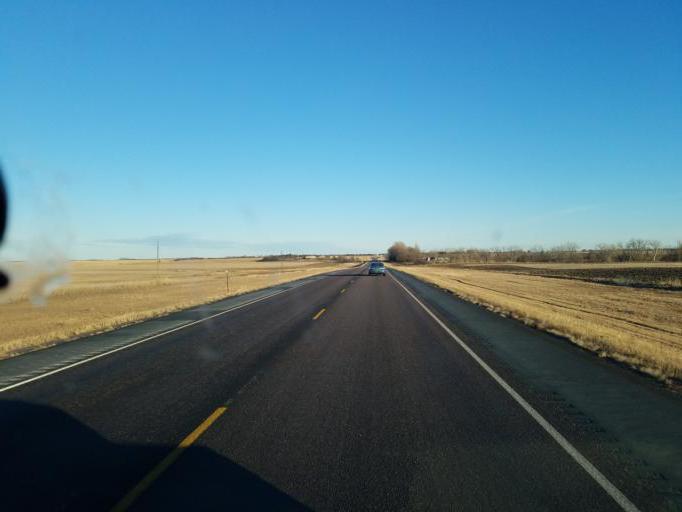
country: US
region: South Dakota
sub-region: Bon Homme County
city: Tyndall
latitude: 42.9957
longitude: -97.9265
